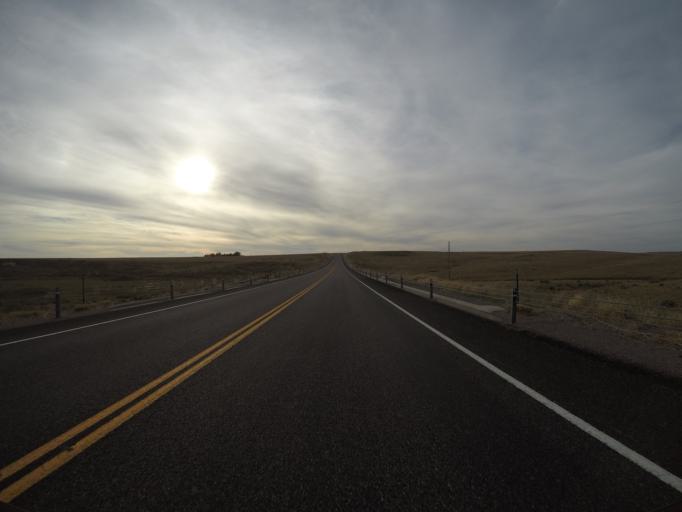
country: US
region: Kansas
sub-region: Cheyenne County
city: Saint Francis
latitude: 39.7467
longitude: -102.0806
